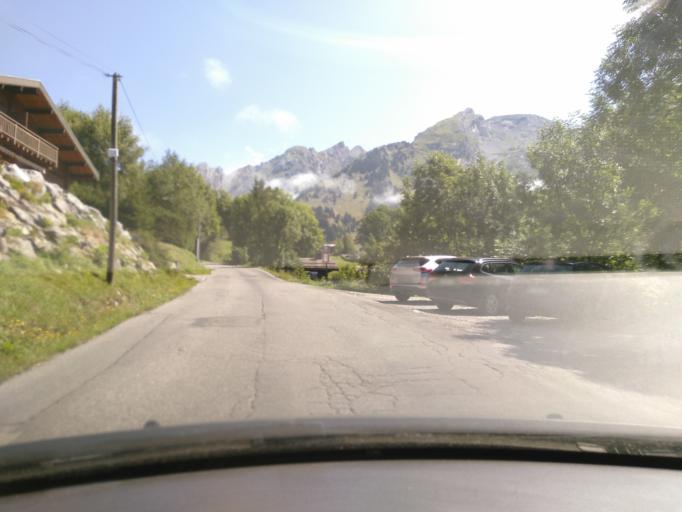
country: FR
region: Rhone-Alpes
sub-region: Departement de la Haute-Savoie
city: La Clusaz
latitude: 45.9114
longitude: 6.4585
